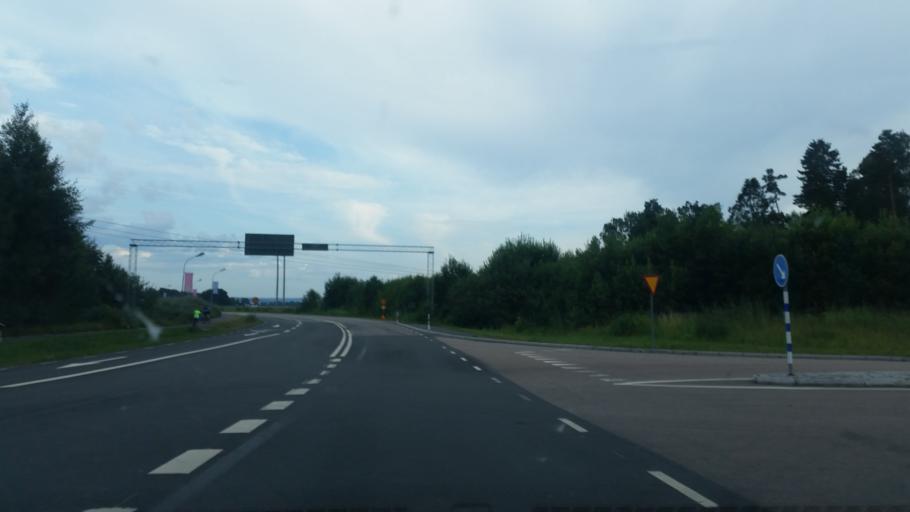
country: SE
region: Vaestra Goetaland
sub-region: Skara Kommun
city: Axvall
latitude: 58.4019
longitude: 13.5512
